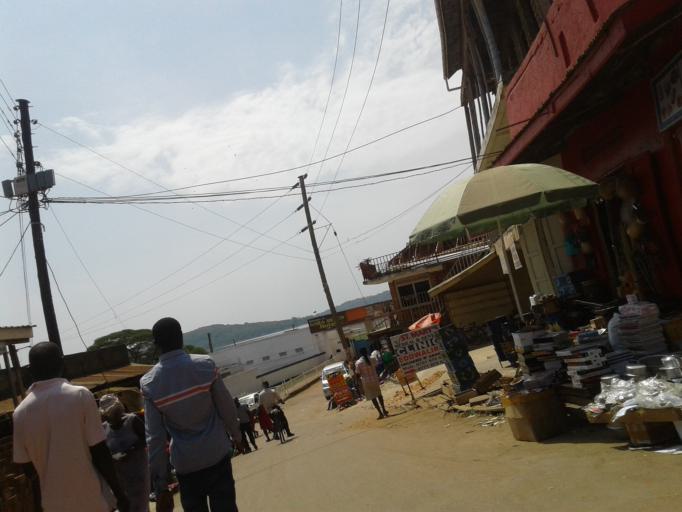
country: UG
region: Central Region
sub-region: Kampala District
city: Kampala
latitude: 0.2563
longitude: 32.6365
